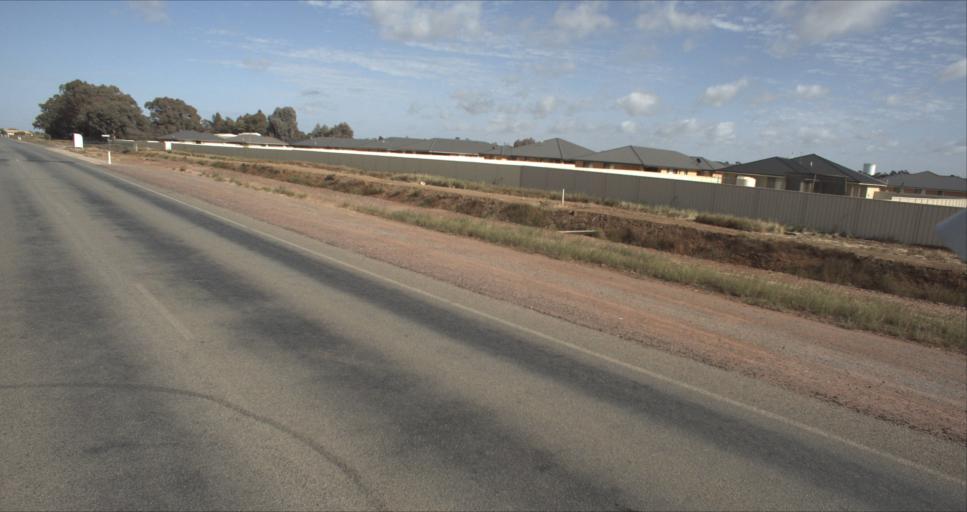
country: AU
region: New South Wales
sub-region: Leeton
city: Leeton
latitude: -34.5712
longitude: 146.3999
